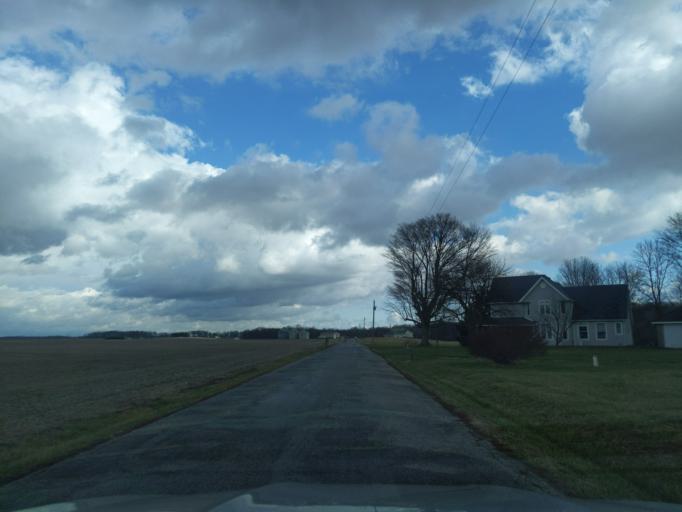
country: US
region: Indiana
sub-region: Decatur County
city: Greensburg
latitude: 39.4117
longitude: -85.5162
